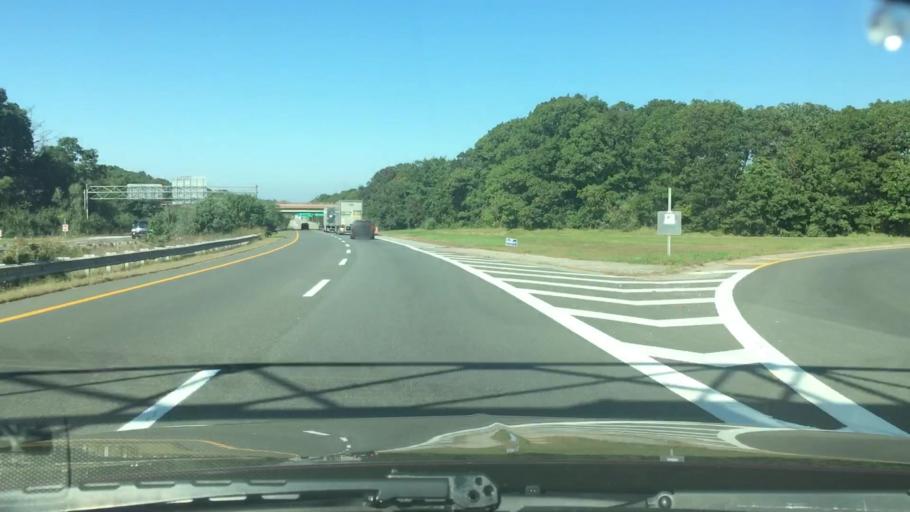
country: US
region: New York
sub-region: Suffolk County
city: Yaphank
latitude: 40.8421
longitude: -72.8888
